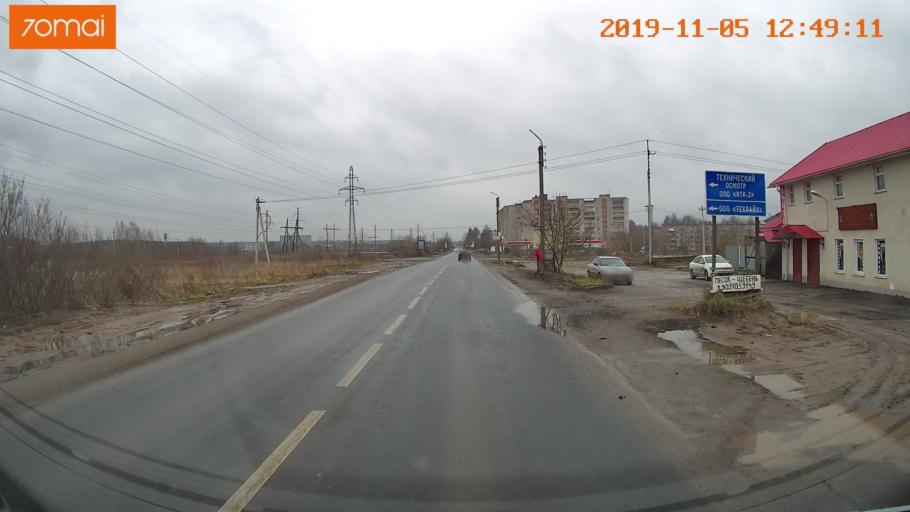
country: RU
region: Ivanovo
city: Kokhma
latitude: 56.9563
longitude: 41.1027
